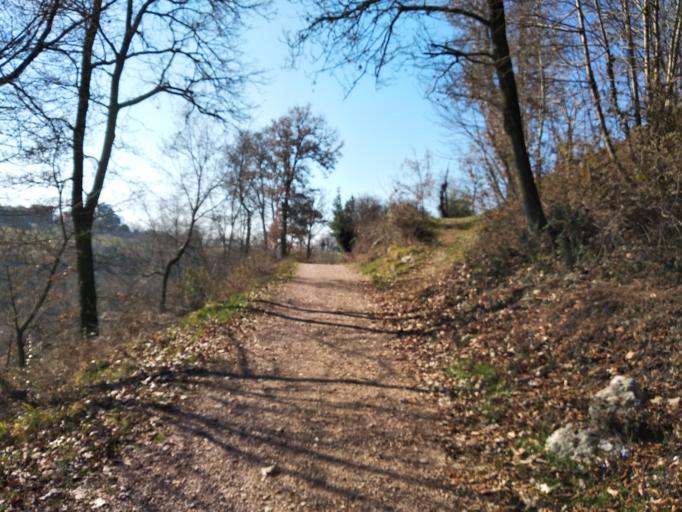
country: IT
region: Veneto
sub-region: Provincia di Vicenza
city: Gambugliano
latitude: 45.5903
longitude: 11.4557
